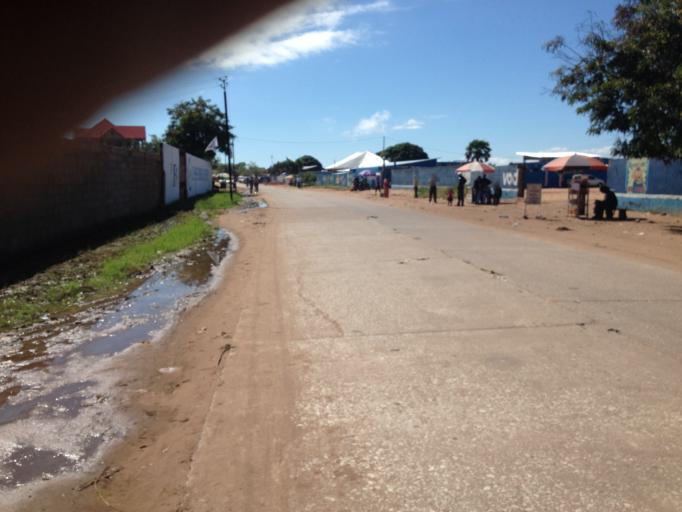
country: CD
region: Katanga
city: Kalemie
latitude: -5.9137
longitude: 29.2025
